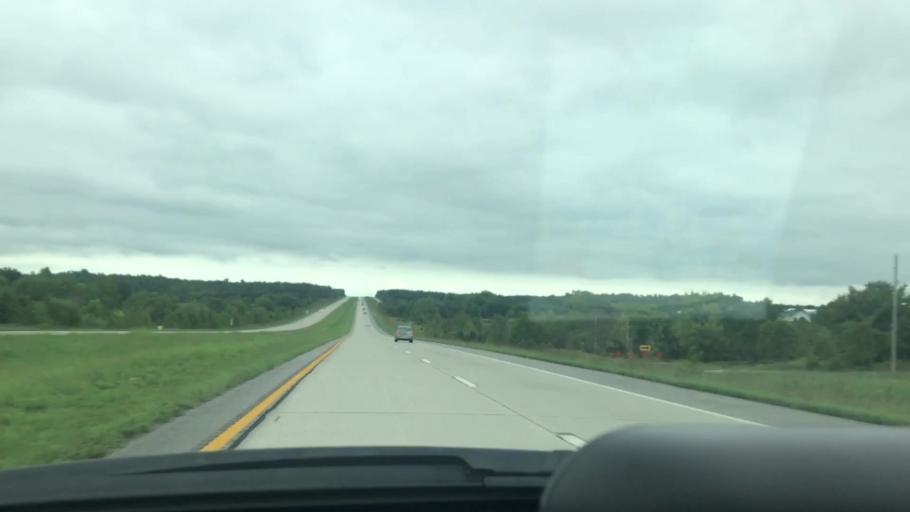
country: US
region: Missouri
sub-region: Greene County
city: Fair Grove
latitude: 37.4637
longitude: -93.1390
